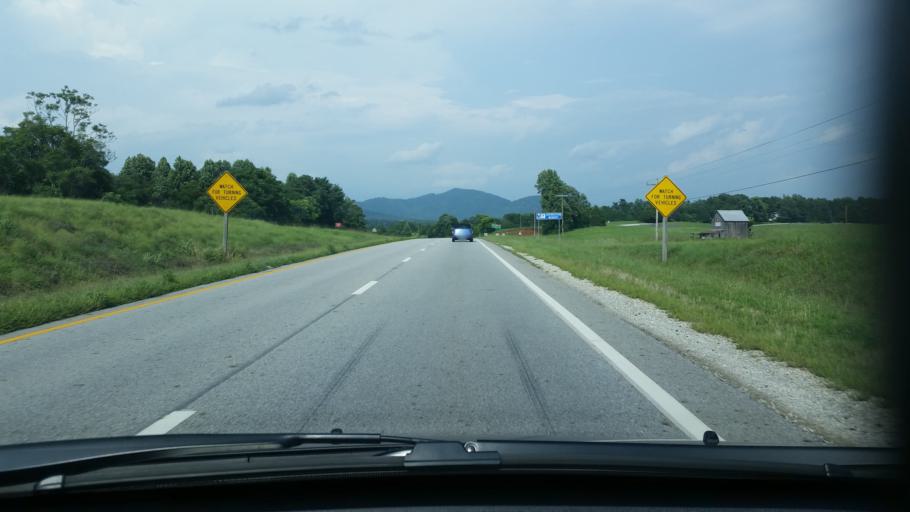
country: US
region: Virginia
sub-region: Nelson County
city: Lovingston
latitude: 37.7150
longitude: -78.9117
